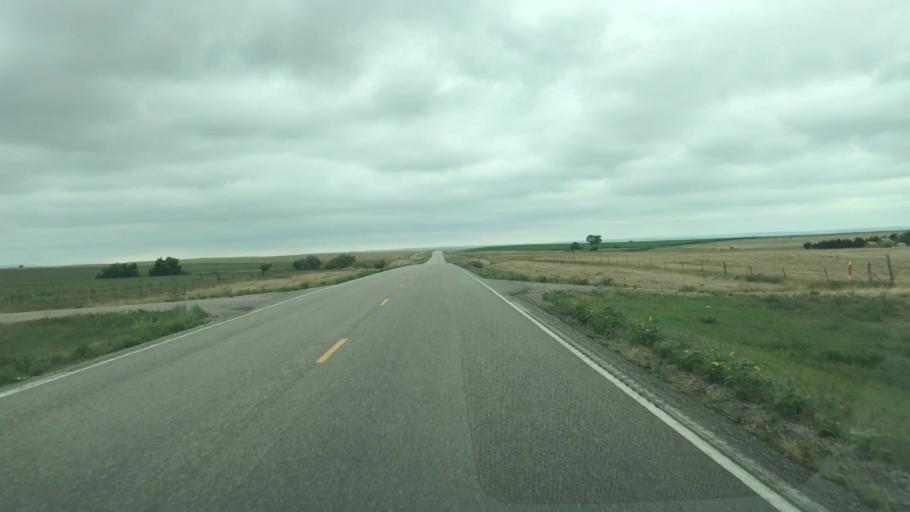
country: US
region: South Dakota
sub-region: Jackson County
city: Kadoka
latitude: 43.8197
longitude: -101.5224
